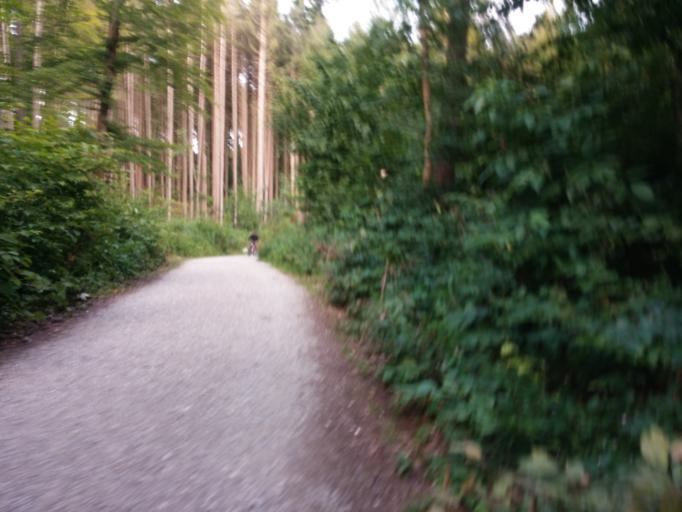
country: DE
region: Bavaria
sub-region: Upper Bavaria
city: Moosach
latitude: 48.0244
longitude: 11.8610
